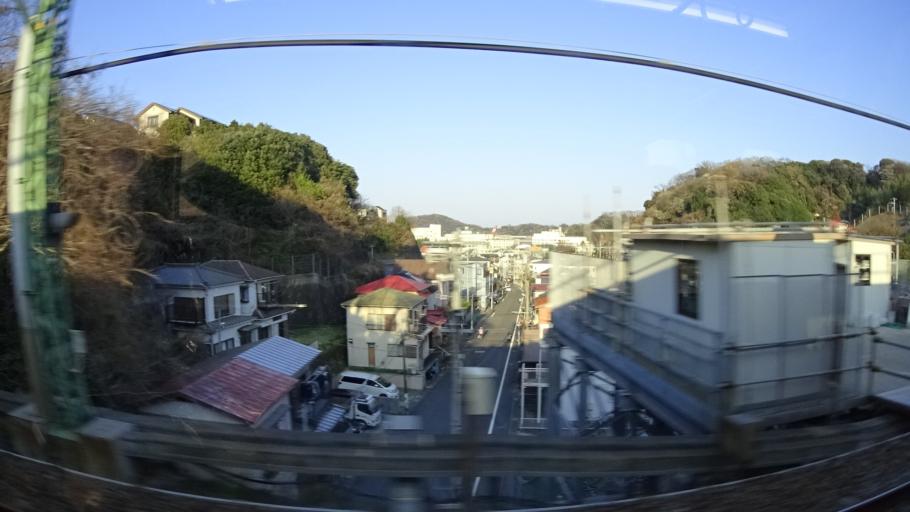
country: JP
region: Kanagawa
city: Yokosuka
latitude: 35.2931
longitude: 139.6275
